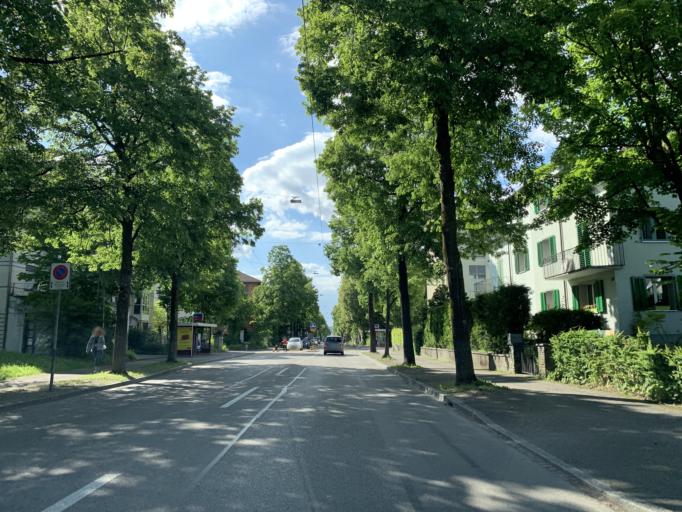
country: CH
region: Zurich
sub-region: Bezirk Winterthur
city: Mattenbach (Kreis 7) / Gutschick
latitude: 47.4877
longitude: 8.7535
